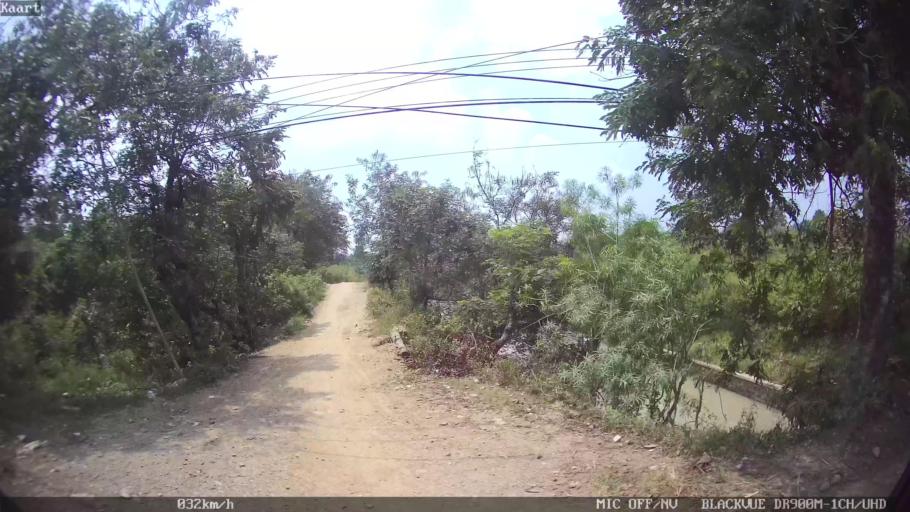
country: ID
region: Lampung
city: Pringsewu
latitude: -5.3532
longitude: 105.0148
